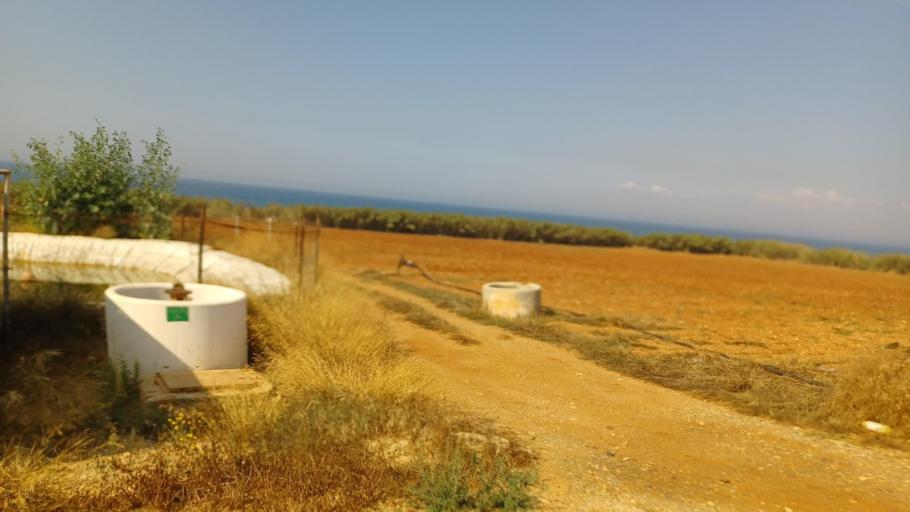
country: CY
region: Larnaka
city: Xylotymbou
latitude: 34.9785
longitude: 33.7858
